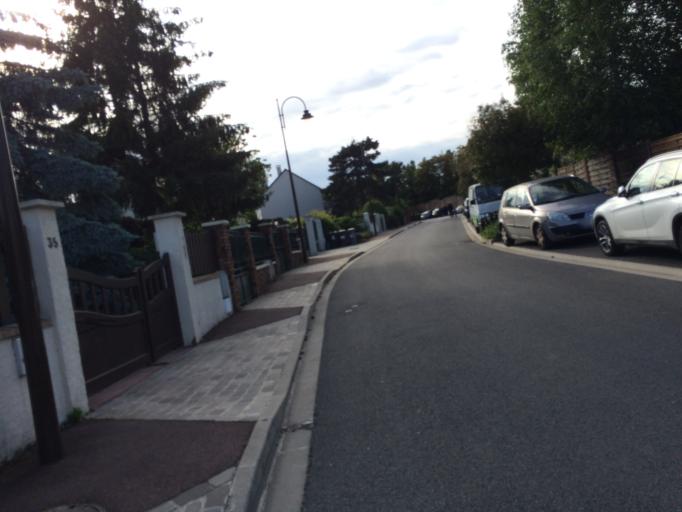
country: FR
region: Ile-de-France
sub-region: Departement des Hauts-de-Seine
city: Chatenay-Malabry
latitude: 48.7589
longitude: 2.2747
